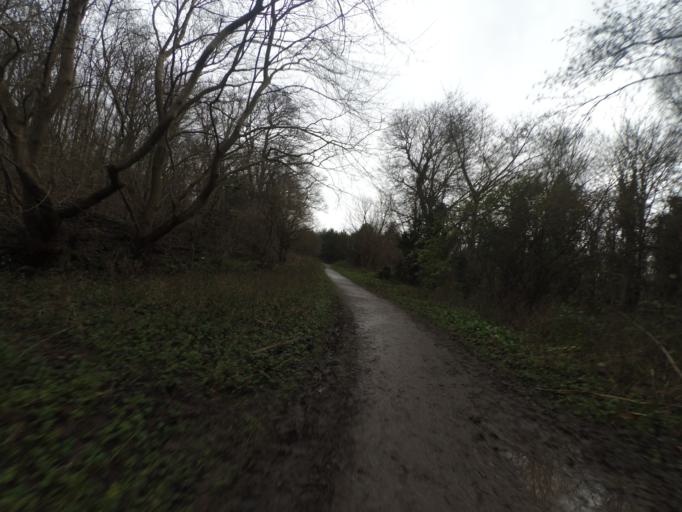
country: GB
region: Scotland
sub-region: West Lothian
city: Seafield
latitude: 55.9278
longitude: -3.1447
